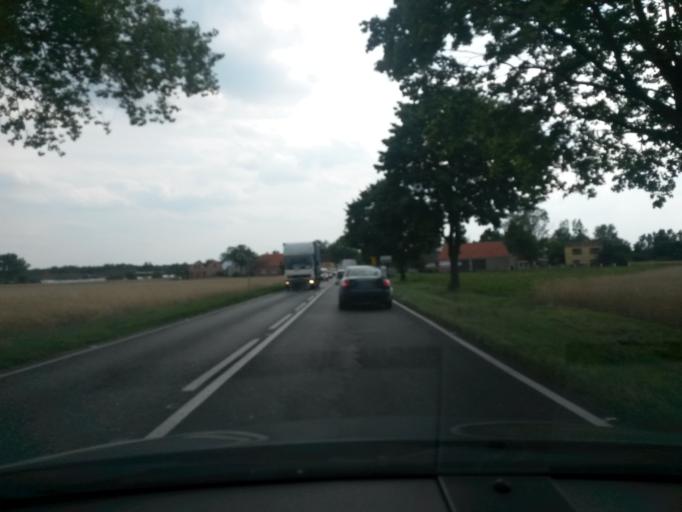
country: PL
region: Greater Poland Voivodeship
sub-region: Powiat poznanski
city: Kornik
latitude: 52.1855
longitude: 17.0556
